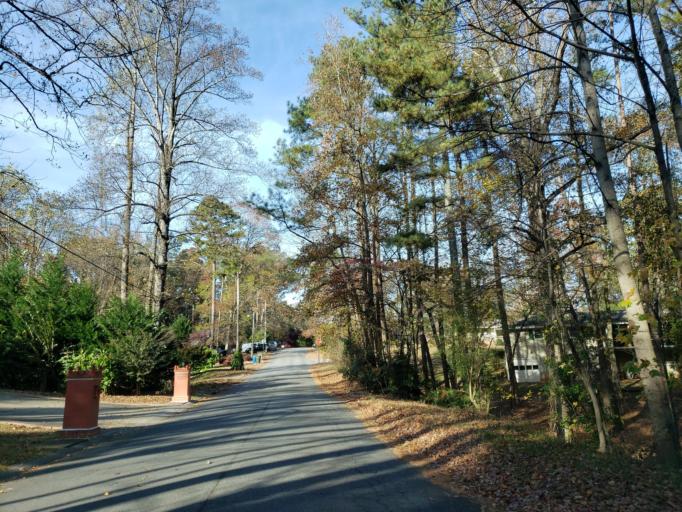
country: US
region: Georgia
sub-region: Cobb County
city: Kennesaw
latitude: 34.0255
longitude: -84.6071
